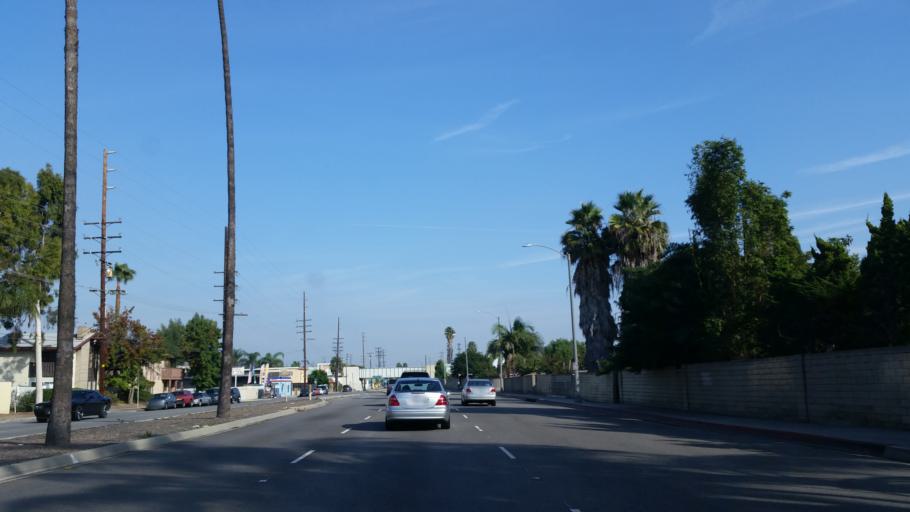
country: US
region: California
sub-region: Los Angeles County
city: Lakewood
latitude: 33.8499
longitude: -118.1675
